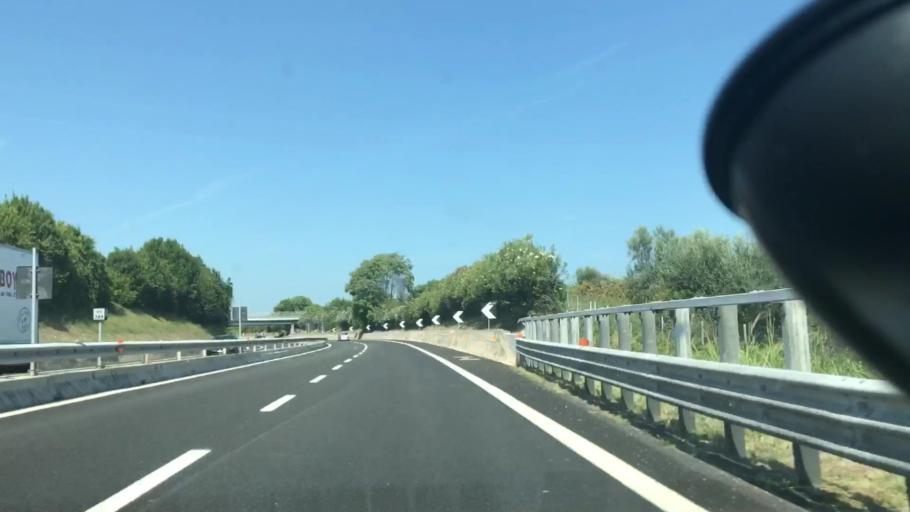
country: IT
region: Abruzzo
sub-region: Provincia di Chieti
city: Tollo
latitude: 42.3560
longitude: 14.3511
